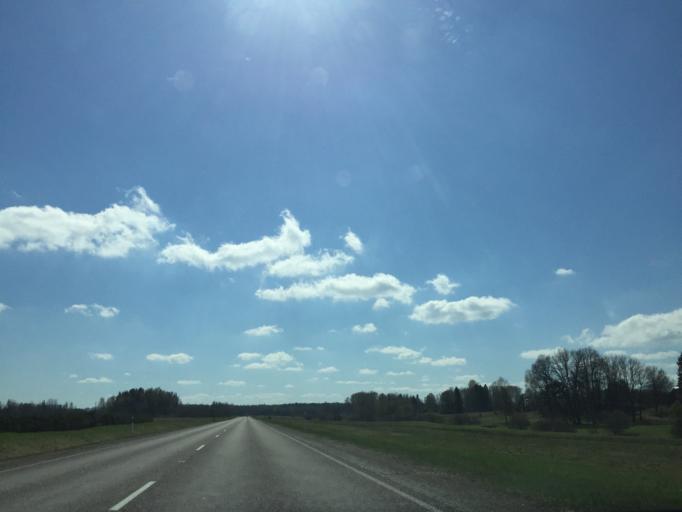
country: EE
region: Valgamaa
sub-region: Torva linn
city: Torva
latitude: 58.0275
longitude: 26.1718
